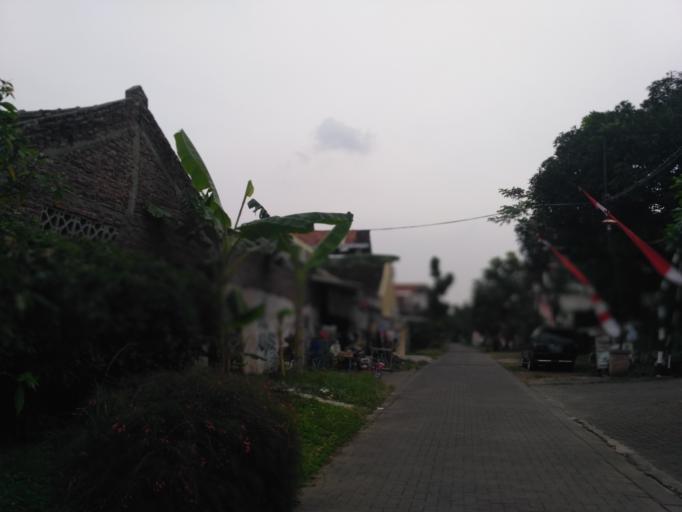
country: ID
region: Central Java
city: Semarang
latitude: -7.0648
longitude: 110.4189
